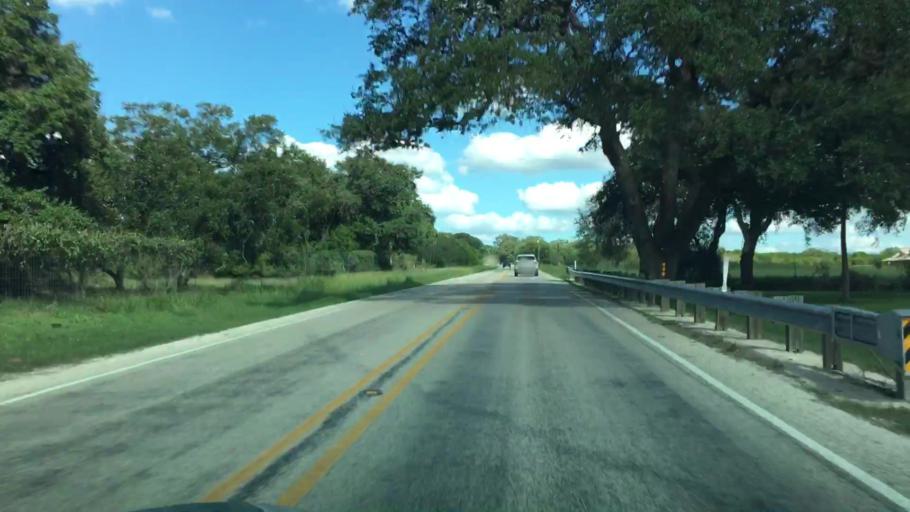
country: US
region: Texas
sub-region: Blanco County
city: Blanco
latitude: 30.0917
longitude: -98.3752
